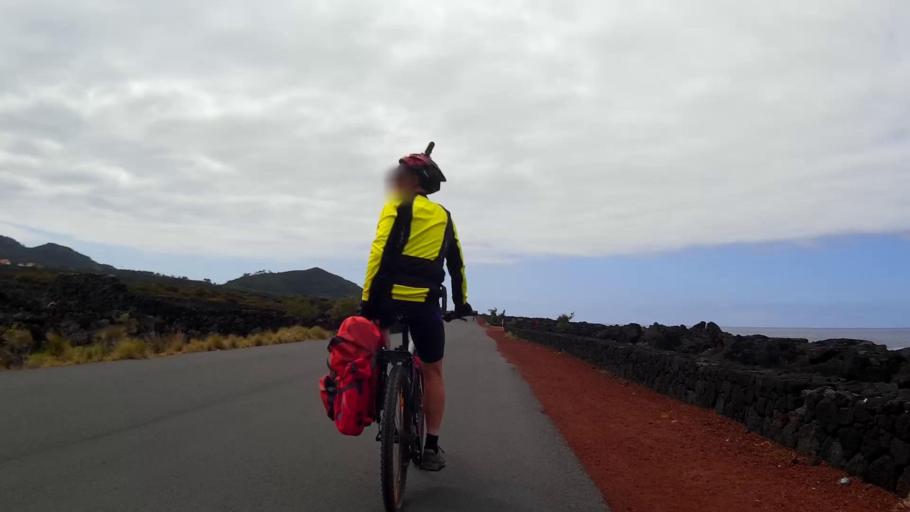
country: PT
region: Azores
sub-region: Madalena
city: Madalena
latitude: 38.5169
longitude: -28.5393
